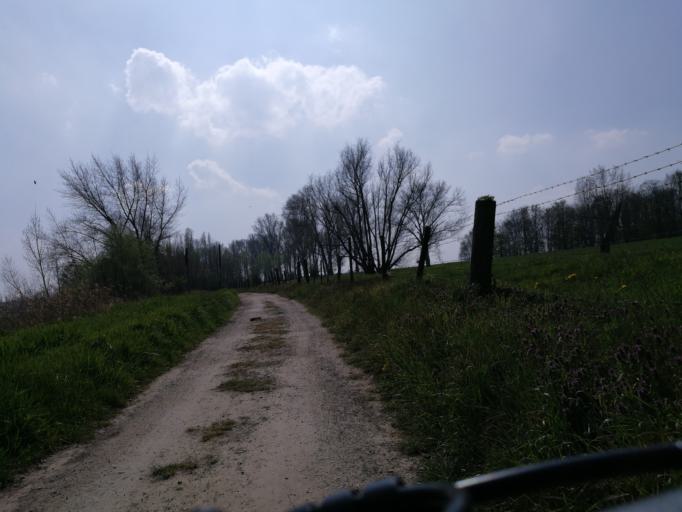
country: DE
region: North Rhine-Westphalia
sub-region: Regierungsbezirk Dusseldorf
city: Dormagen
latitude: 51.1432
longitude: 6.8462
